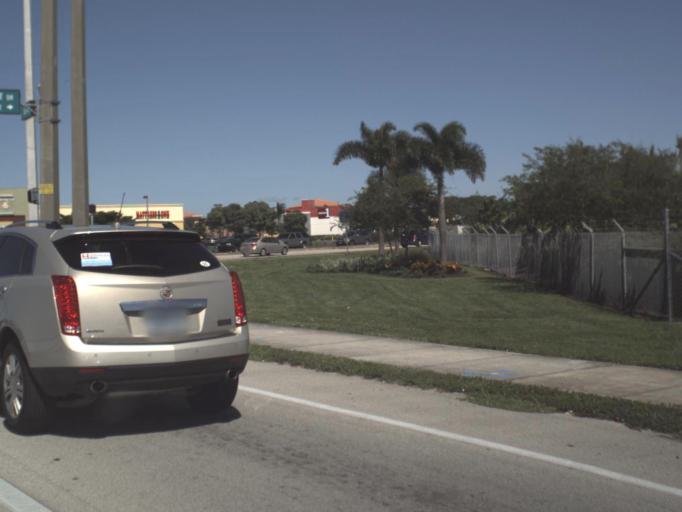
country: US
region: Florida
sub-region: Lee County
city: Pine Manor
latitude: 26.5823
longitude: -81.8718
